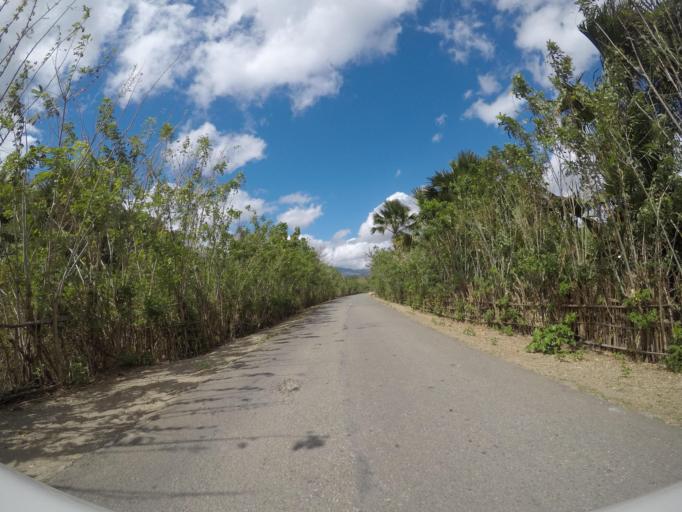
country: TL
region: Lautem
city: Lospalos
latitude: -8.4602
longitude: 126.8218
